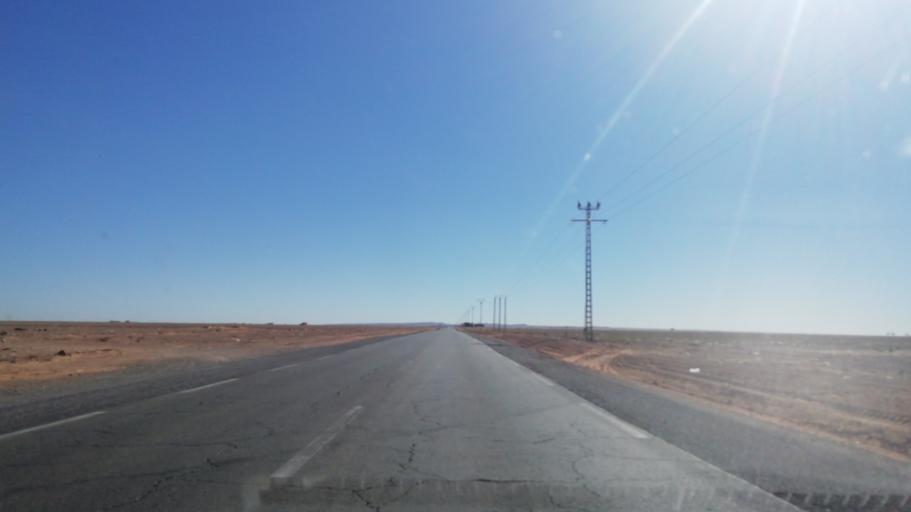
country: DZ
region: Saida
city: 'Ain el Hadjar
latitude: 34.0174
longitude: 0.1085
